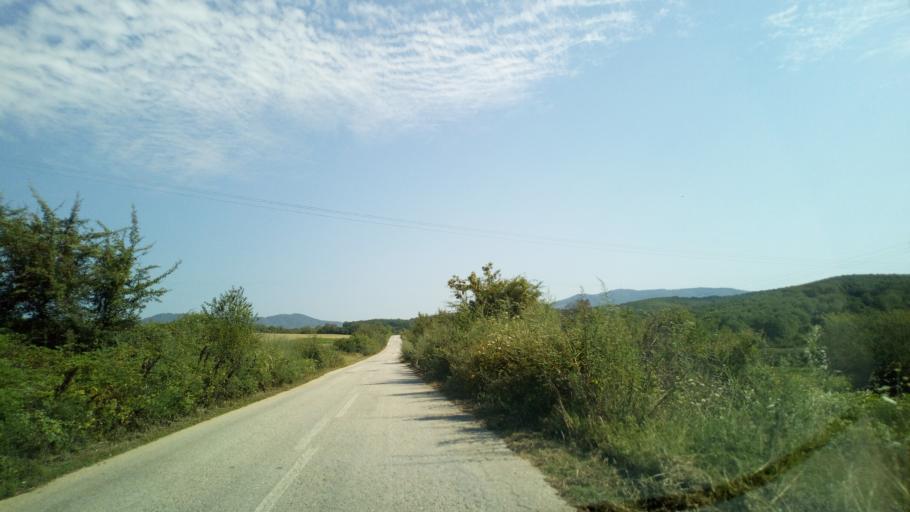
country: GR
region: Central Macedonia
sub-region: Nomos Thessalonikis
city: Askos
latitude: 40.7668
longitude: 23.3769
